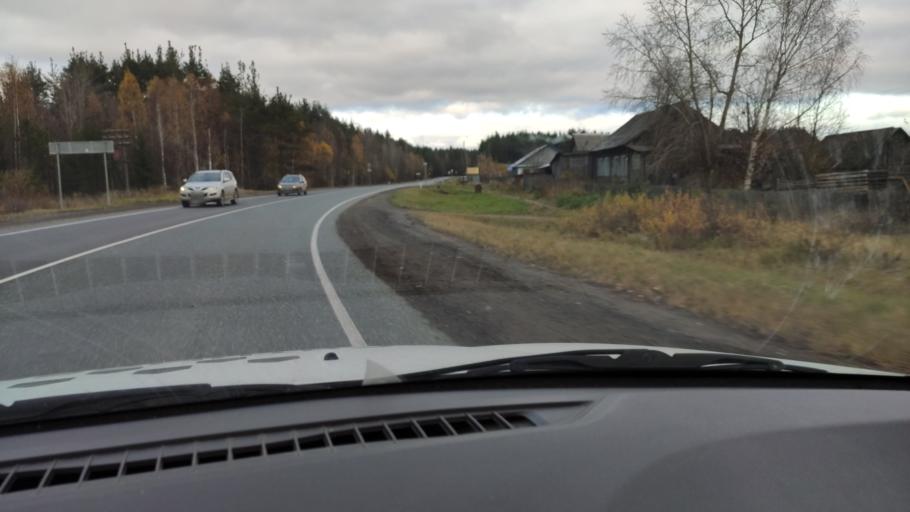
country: RU
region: Kirov
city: Belaya Kholunitsa
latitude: 58.8698
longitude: 50.8441
